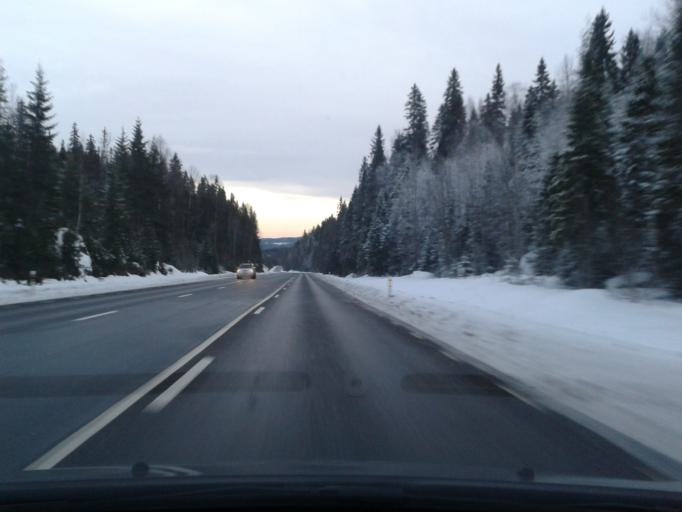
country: SE
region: Vaesternorrland
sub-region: Kramfors Kommun
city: Bollstabruk
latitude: 63.1158
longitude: 17.4944
